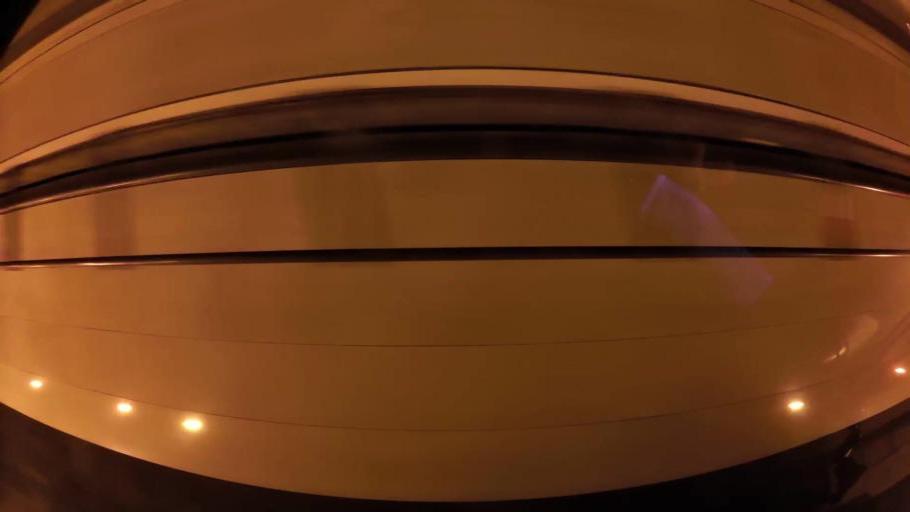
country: EC
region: Pichincha
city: Quito
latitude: -0.2182
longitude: -78.5196
